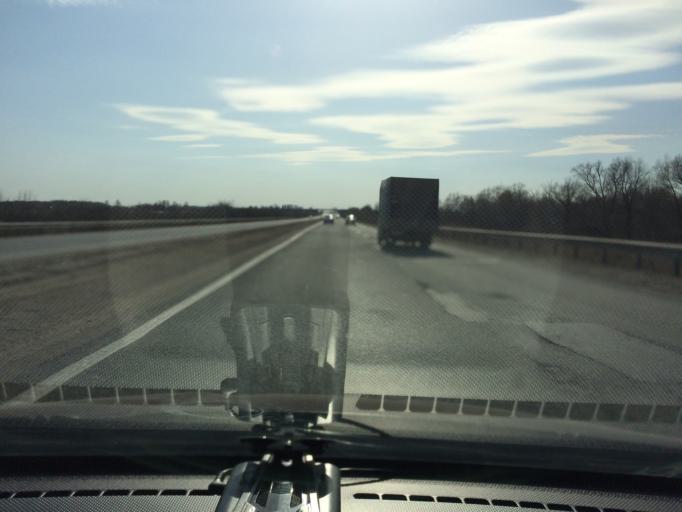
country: RU
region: Mariy-El
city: Yoshkar-Ola
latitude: 56.6861
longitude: 48.0395
